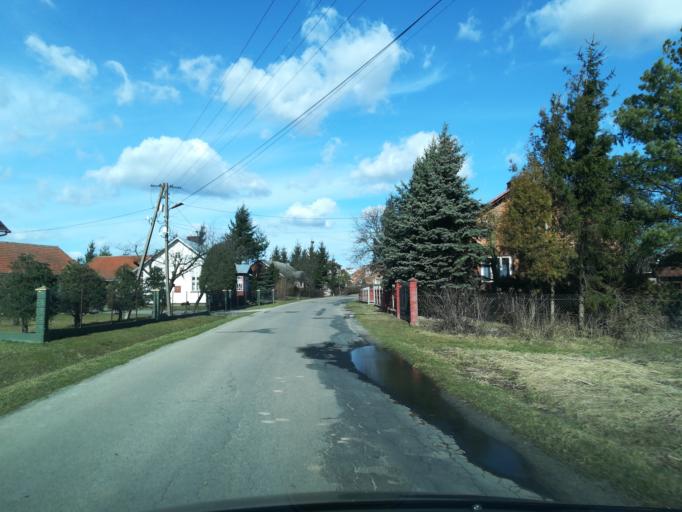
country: PL
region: Subcarpathian Voivodeship
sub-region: Powiat lancucki
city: Kosina
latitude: 50.0854
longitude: 22.3225
